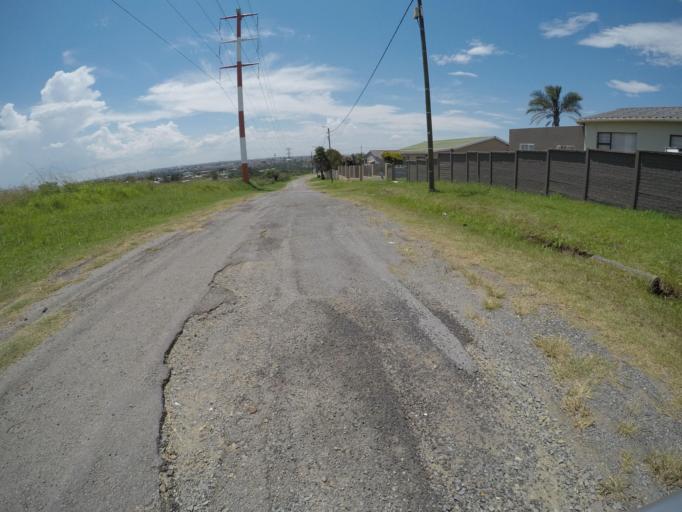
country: ZA
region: Eastern Cape
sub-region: Buffalo City Metropolitan Municipality
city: East London
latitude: -33.0327
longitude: 27.8480
